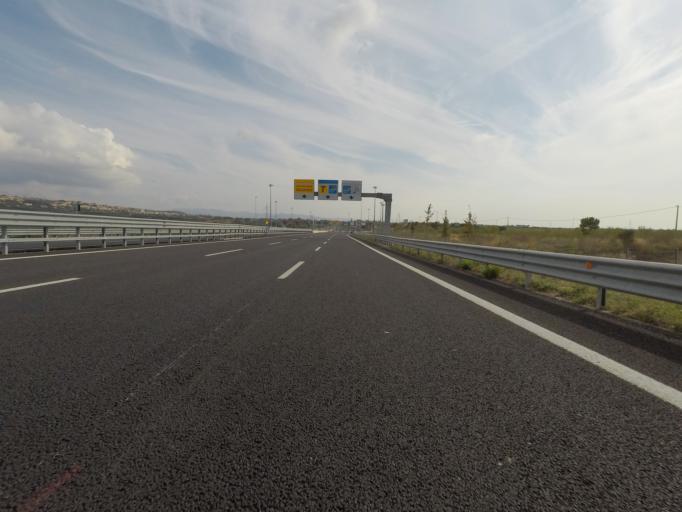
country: IT
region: Latium
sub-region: Provincia di Viterbo
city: Tarquinia
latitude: 42.2594
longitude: 11.7255
